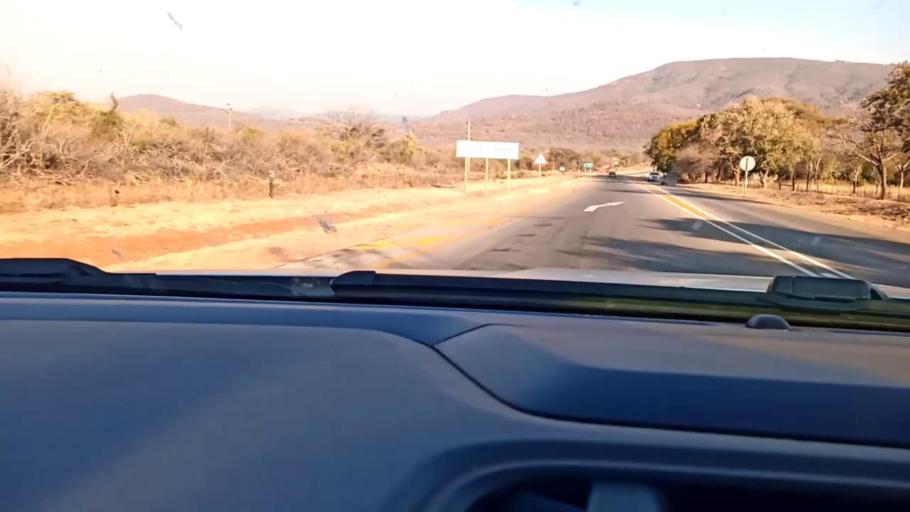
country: ZA
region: Limpopo
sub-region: Mopani District Municipality
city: Duiwelskloof
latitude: -23.6229
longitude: 30.1280
